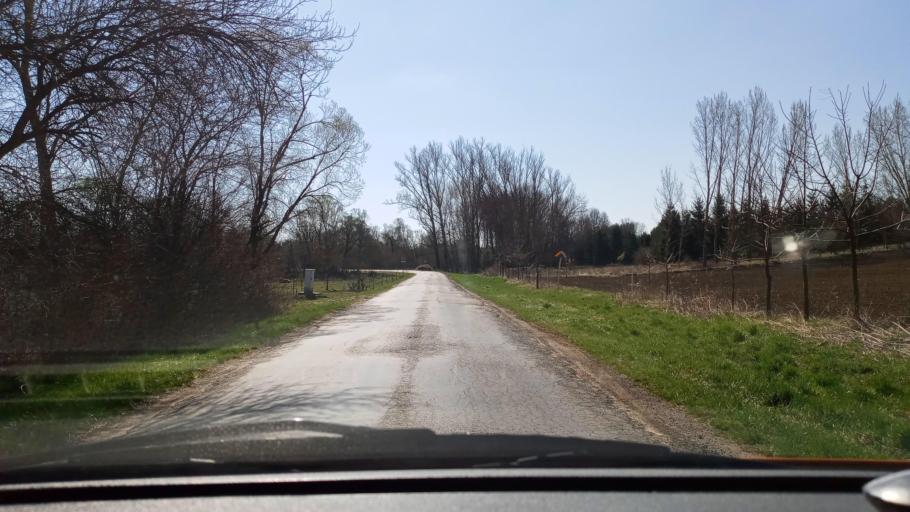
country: HU
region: Baranya
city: Kozarmisleny
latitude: 46.0682
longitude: 18.3674
